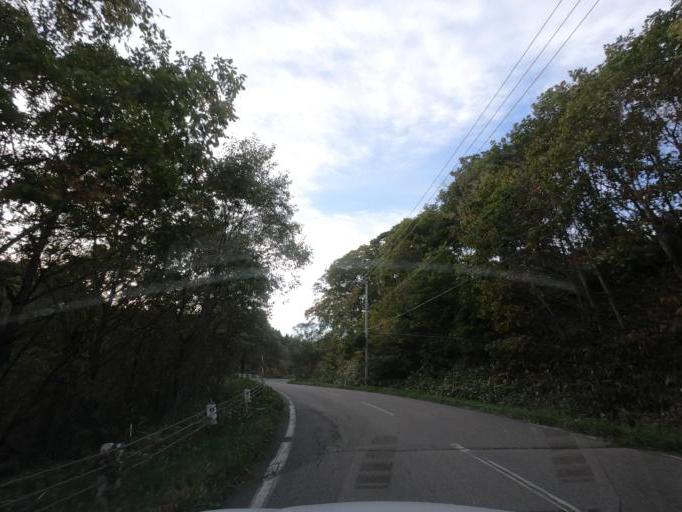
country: JP
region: Hokkaido
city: Obihiro
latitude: 42.5383
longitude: 143.4290
